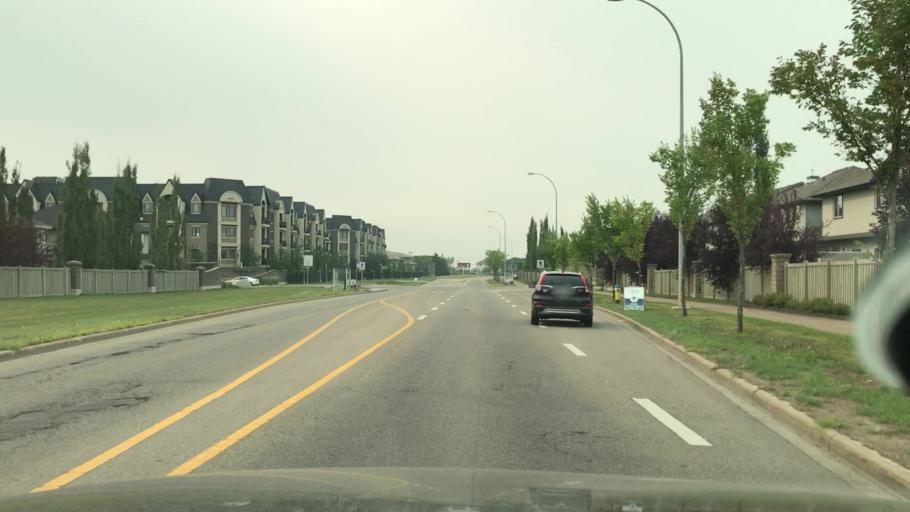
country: CA
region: Alberta
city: Edmonton
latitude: 53.4423
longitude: -113.5658
